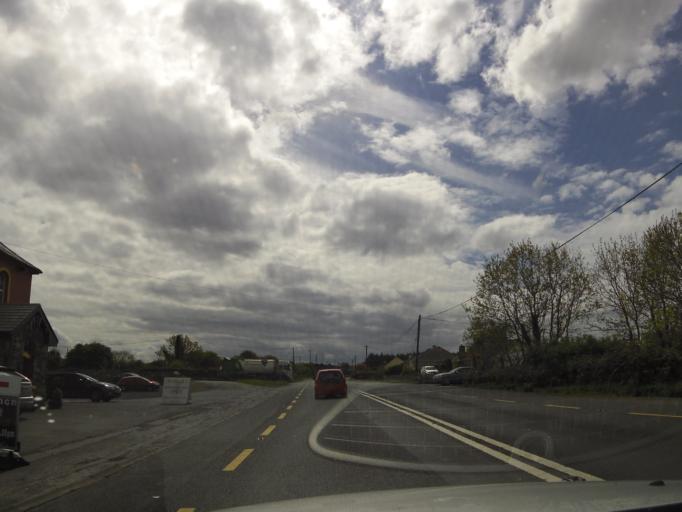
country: IE
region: Connaught
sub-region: County Galway
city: Claregalway
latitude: 53.3139
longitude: -8.9861
